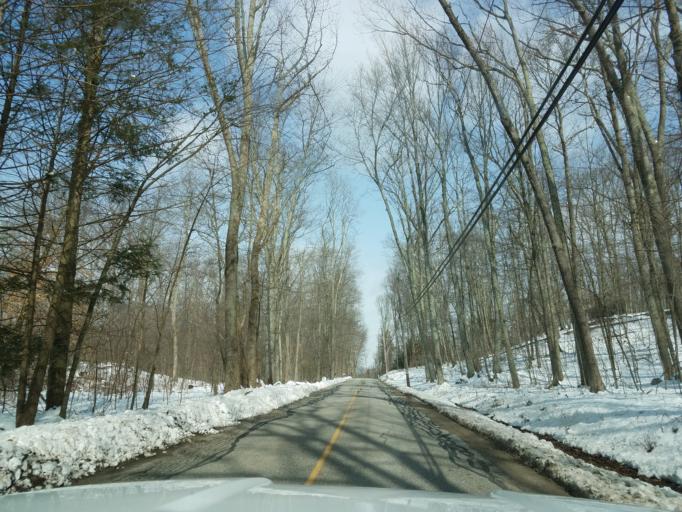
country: US
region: Connecticut
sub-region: Tolland County
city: Coventry Lake
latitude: 41.7222
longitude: -72.3551
